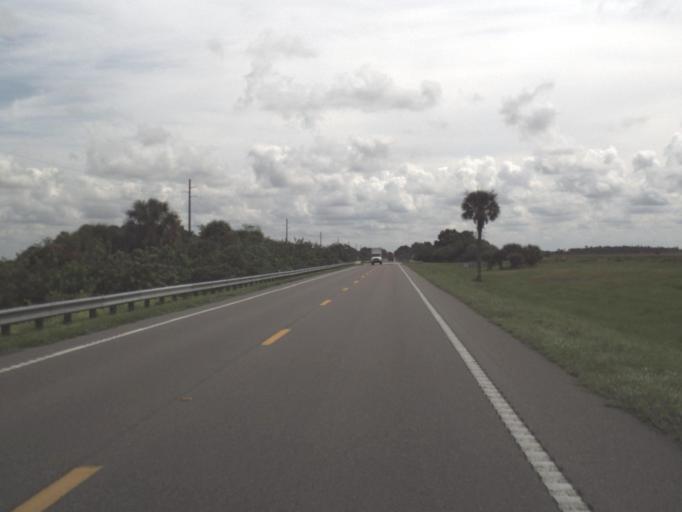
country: US
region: Florida
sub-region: Highlands County
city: Lake Placid
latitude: 27.2098
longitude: -81.1520
